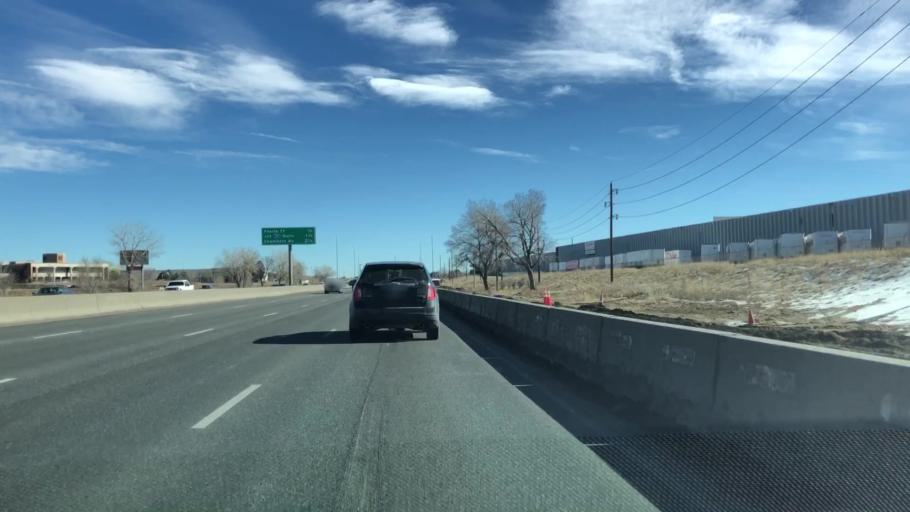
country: US
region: Colorado
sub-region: Adams County
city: Aurora
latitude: 39.7746
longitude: -104.8580
